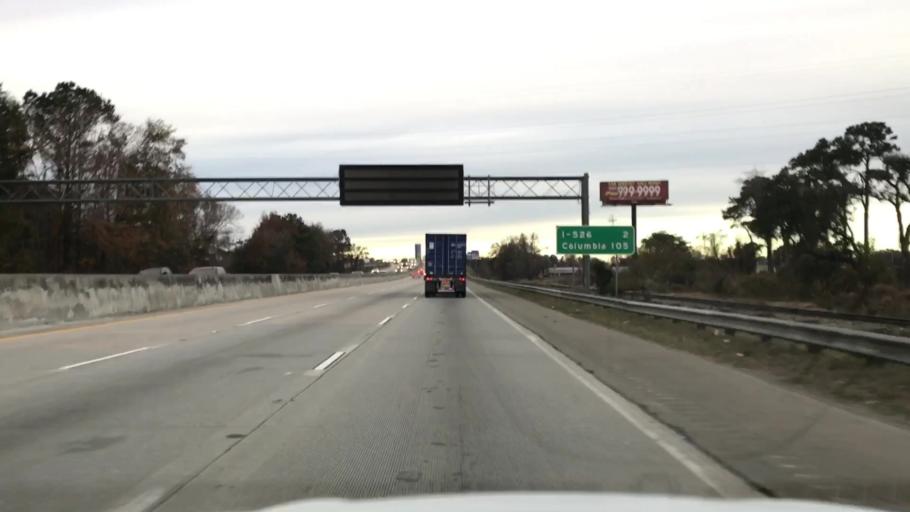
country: US
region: South Carolina
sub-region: Charleston County
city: North Charleston
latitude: 32.8618
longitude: -79.9948
